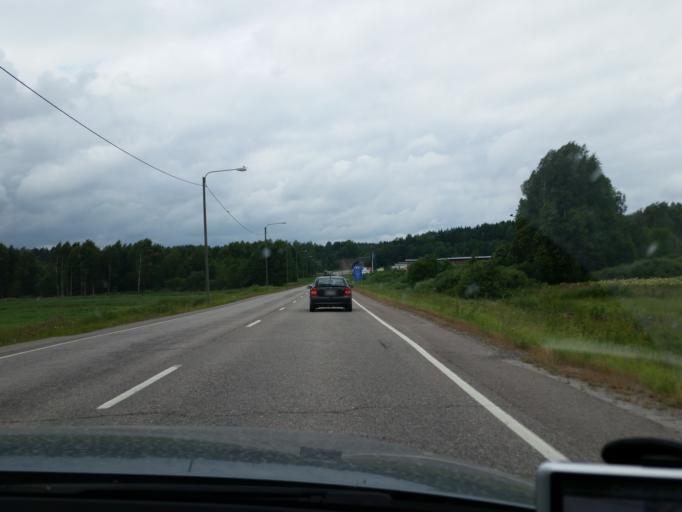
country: FI
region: Uusimaa
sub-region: Helsinki
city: Vihti
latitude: 60.3075
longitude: 24.2530
